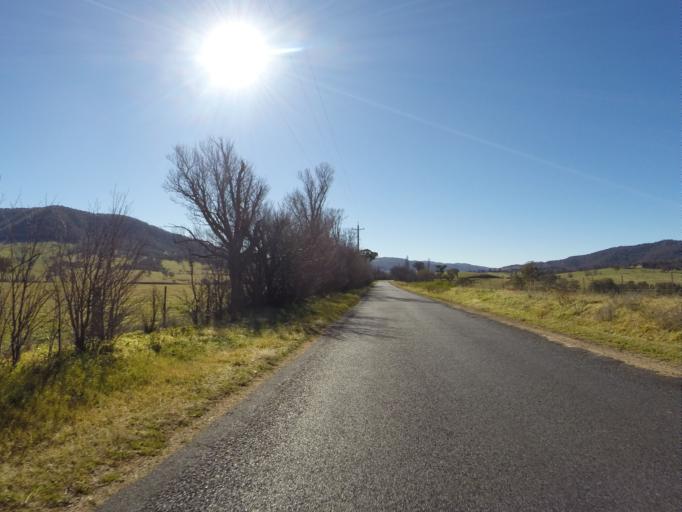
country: AU
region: New South Wales
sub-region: Oberon
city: Oberon
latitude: -33.5373
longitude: 149.8864
